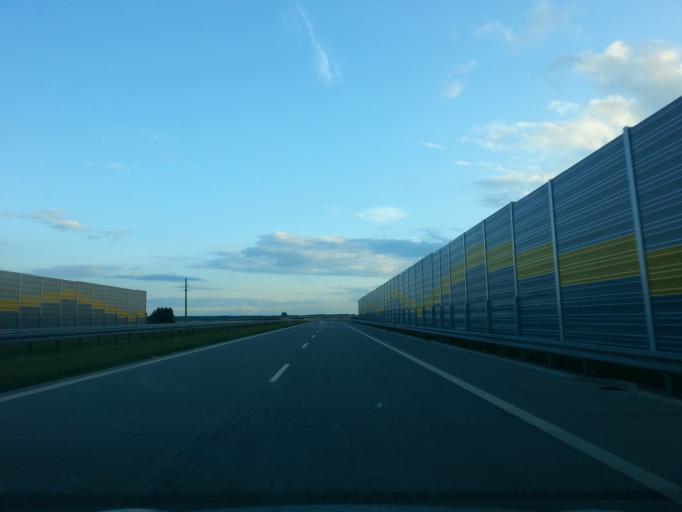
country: PL
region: Lodz Voivodeship
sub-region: Powiat sieradzki
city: Brzeznio
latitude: 51.4810
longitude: 18.6734
